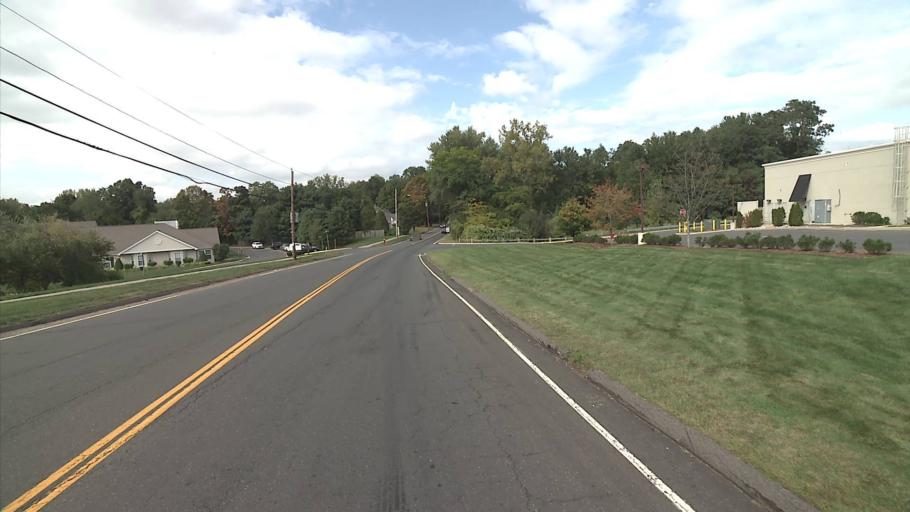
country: US
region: Connecticut
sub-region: Hartford County
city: Newington
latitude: 41.6708
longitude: -72.7184
